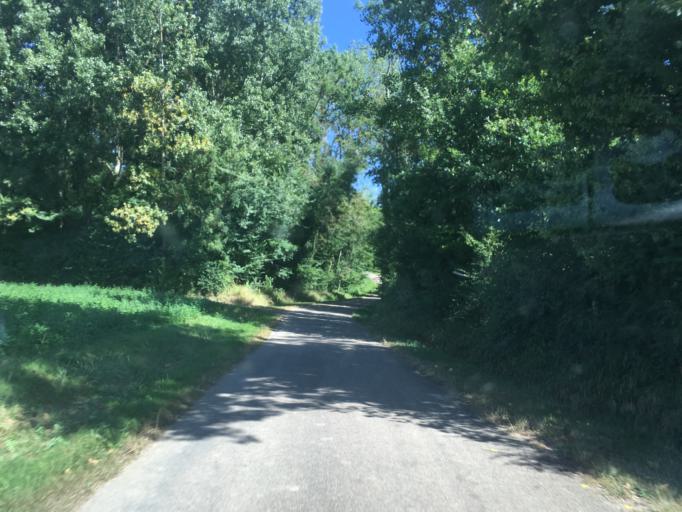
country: FR
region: Bourgogne
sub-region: Departement de l'Yonne
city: Fleury-la-Vallee
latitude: 47.8673
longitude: 3.4403
